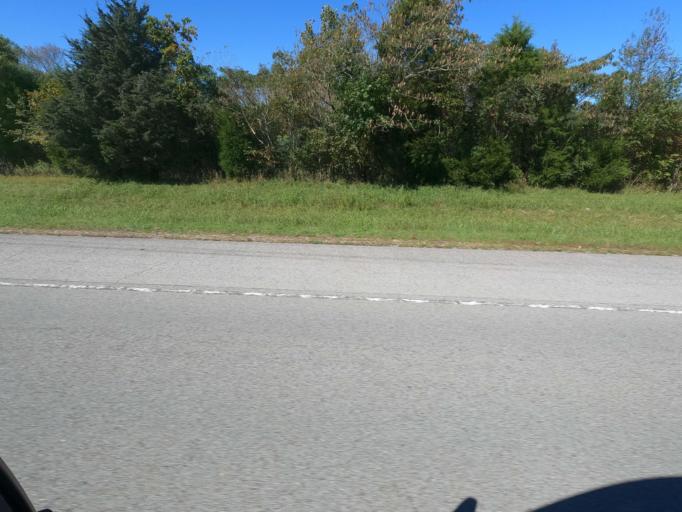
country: US
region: Tennessee
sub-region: Maury County
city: Mount Pleasant
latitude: 35.5086
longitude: -87.2261
